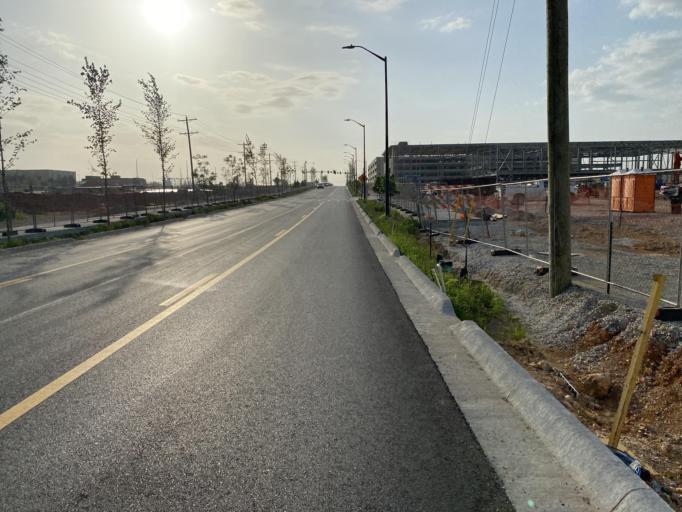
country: US
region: Arkansas
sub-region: Benton County
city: Bentonville
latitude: 36.3675
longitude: -94.1951
